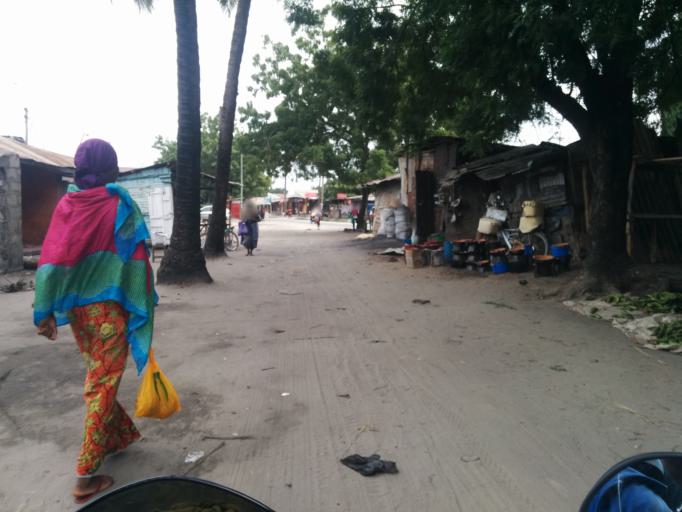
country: TZ
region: Dar es Salaam
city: Dar es Salaam
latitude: -6.8633
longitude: 39.2520
